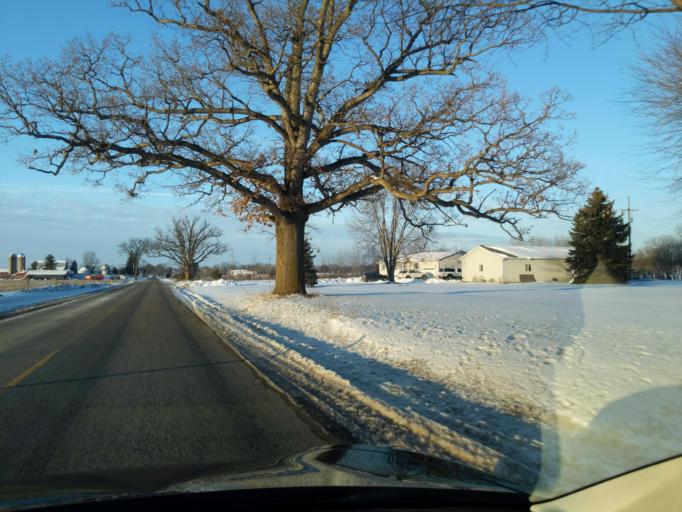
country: US
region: Michigan
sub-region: Ingham County
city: Stockbridge
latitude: 42.5467
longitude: -84.1127
